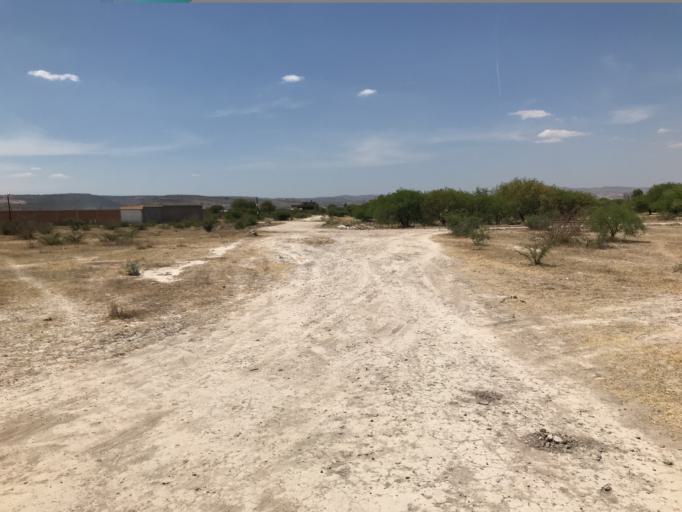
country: MX
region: Durango
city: Victoria de Durango
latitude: 23.9803
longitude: -104.6829
